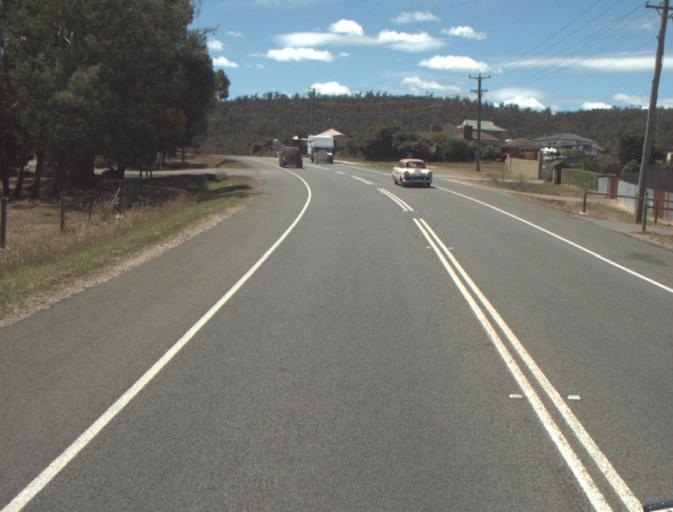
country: AU
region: Tasmania
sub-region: Launceston
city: Mayfield
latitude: -41.3712
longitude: 147.1389
